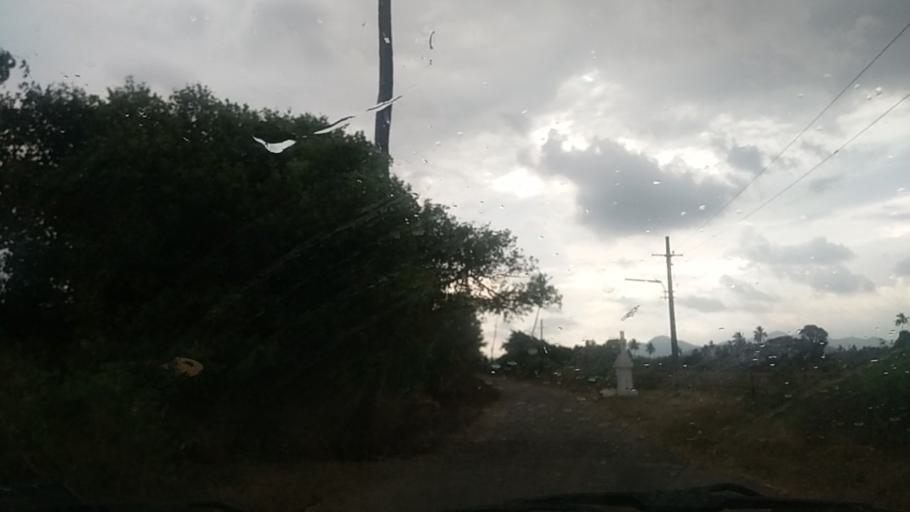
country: IN
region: Goa
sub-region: South Goa
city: Cuncolim
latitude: 15.1904
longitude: 73.9891
